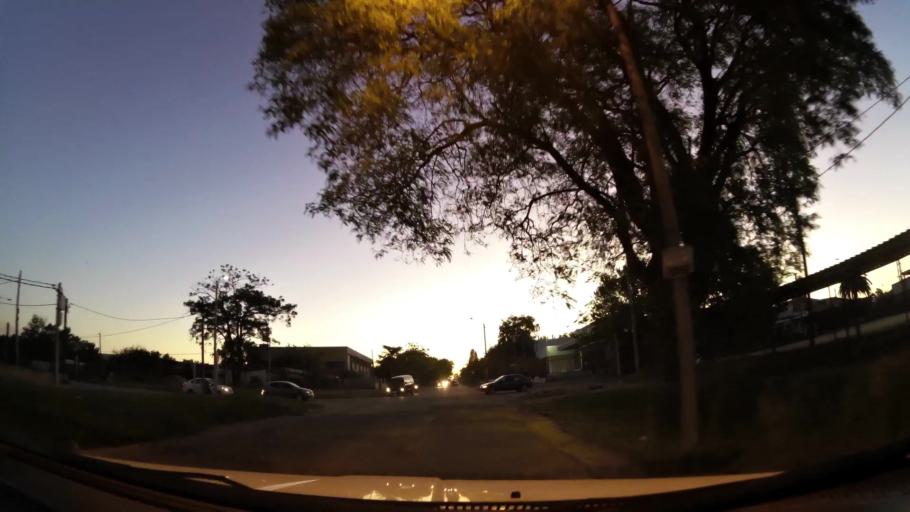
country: UY
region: Montevideo
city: Montevideo
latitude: -34.8335
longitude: -56.1896
